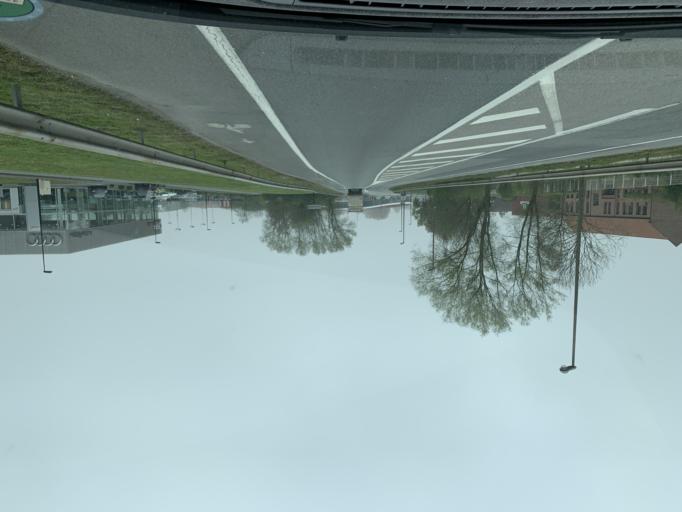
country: FR
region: Nord-Pas-de-Calais
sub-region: Departement du Nord
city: Cappelle-la-Grande
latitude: 51.0172
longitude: 2.3563
